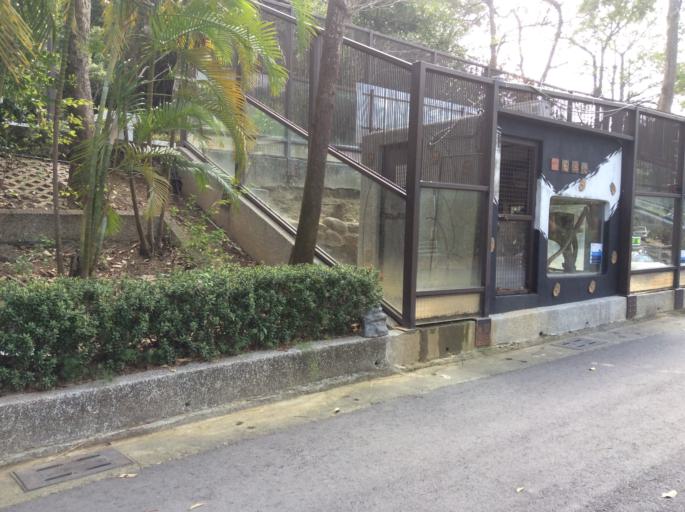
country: TW
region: Kaohsiung
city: Kaohsiung
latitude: 22.6351
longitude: 120.2759
